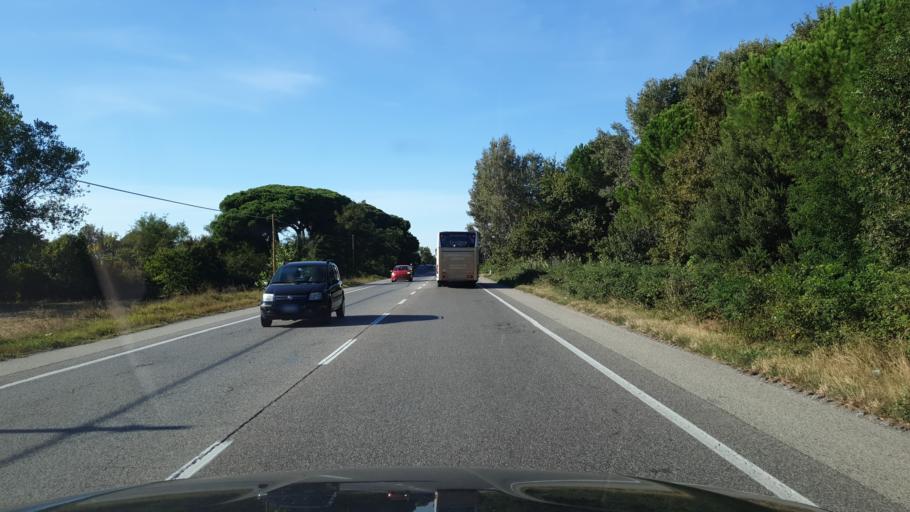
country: IT
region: Emilia-Romagna
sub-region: Provincia di Ravenna
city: Cervia
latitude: 44.2781
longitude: 12.3202
